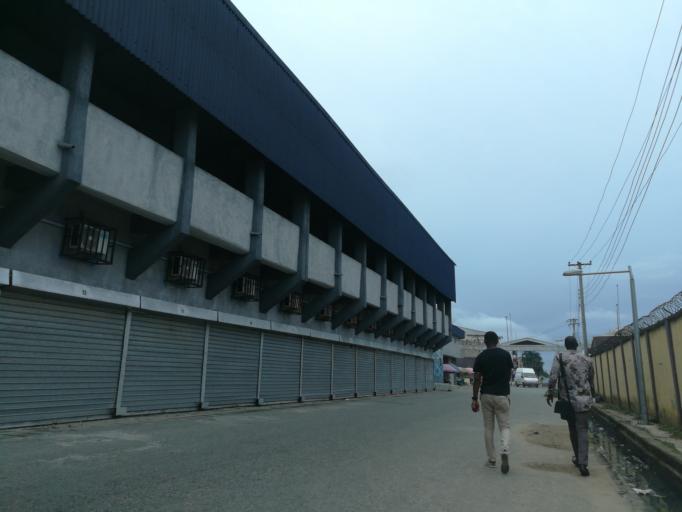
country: NG
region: Rivers
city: Port Harcourt
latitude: 4.7655
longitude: 7.0215
